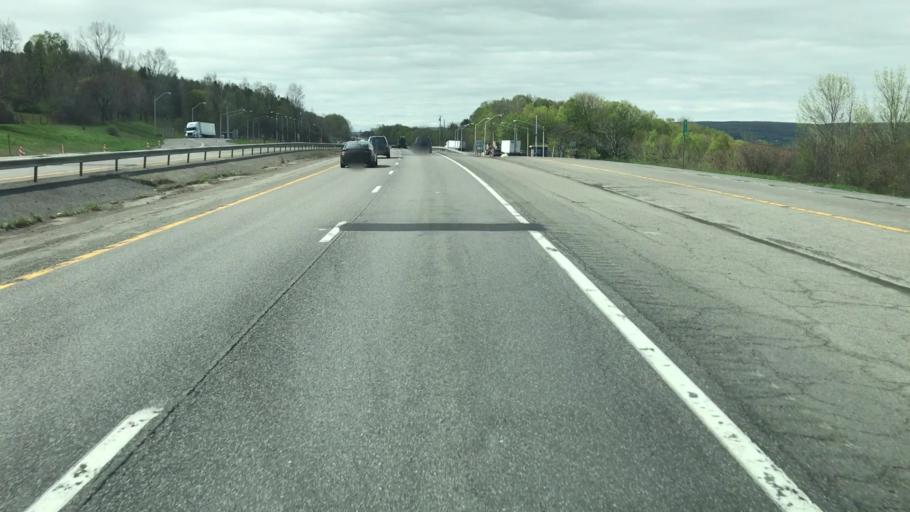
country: US
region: New York
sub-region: Onondaga County
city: Nedrow
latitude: 42.8598
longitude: -76.1178
